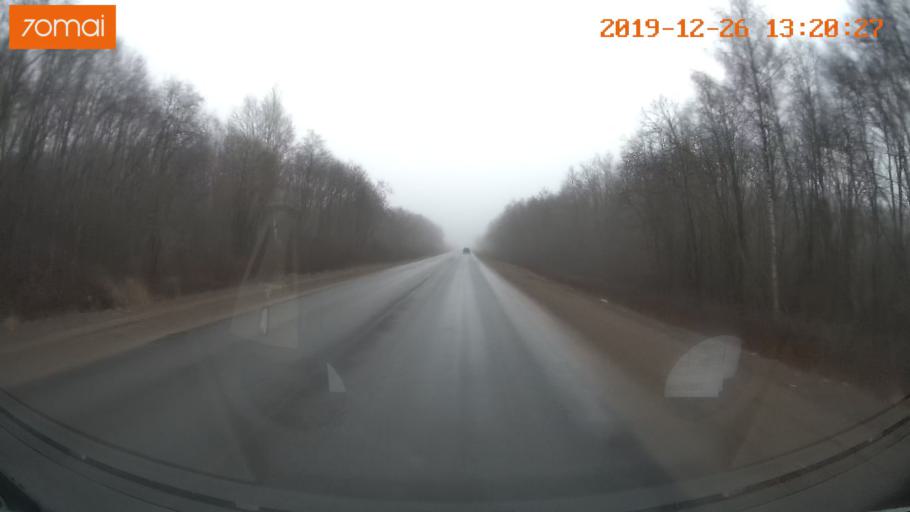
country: RU
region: Vologda
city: Cherepovets
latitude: 58.9270
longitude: 38.1437
